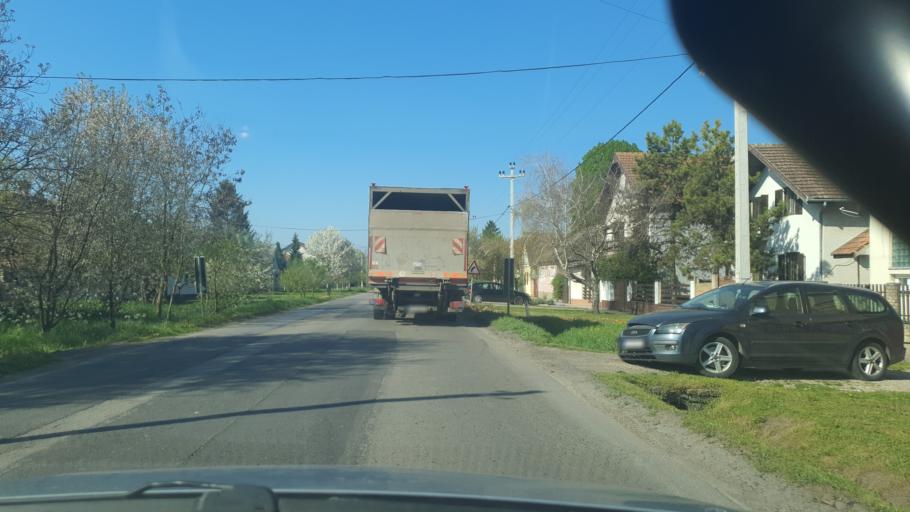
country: RS
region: Autonomna Pokrajina Vojvodina
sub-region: Zapadnobacki Okrug
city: Sombor
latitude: 45.7682
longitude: 19.2654
